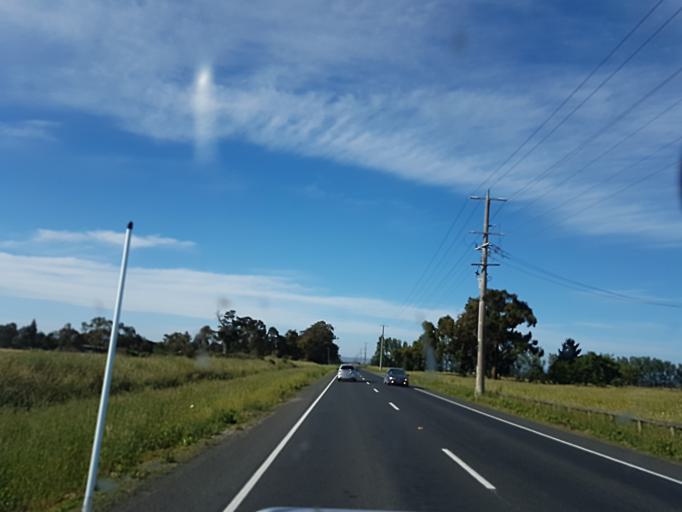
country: AU
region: Victoria
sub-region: Cardinia
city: Koo-Wee-Rup
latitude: -38.1633
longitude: 145.4833
